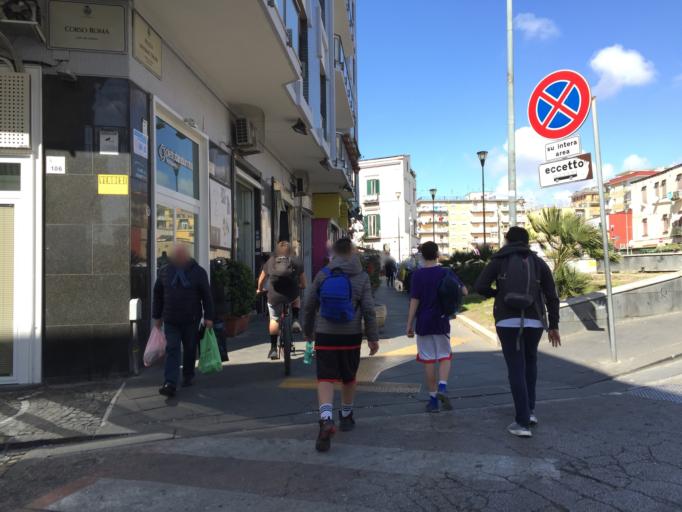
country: IT
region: Campania
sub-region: Provincia di Napoli
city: San Giorgio a Cremano
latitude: 40.8312
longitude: 14.3383
